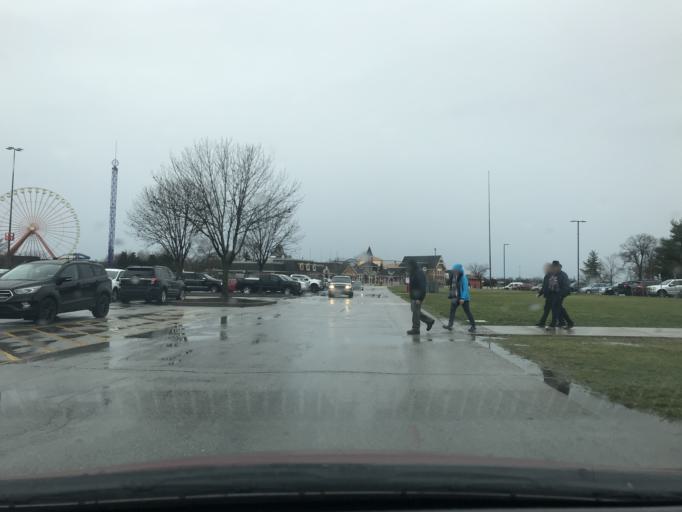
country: US
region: Kentucky
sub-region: Jefferson County
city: Audubon Park
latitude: 38.1983
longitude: -85.7427
